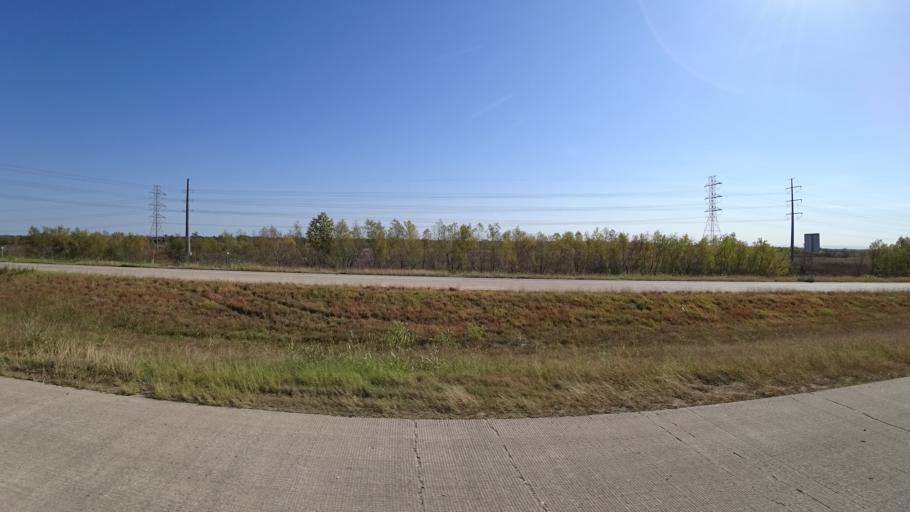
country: US
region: Texas
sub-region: Travis County
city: Hornsby Bend
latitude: 30.2442
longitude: -97.6106
